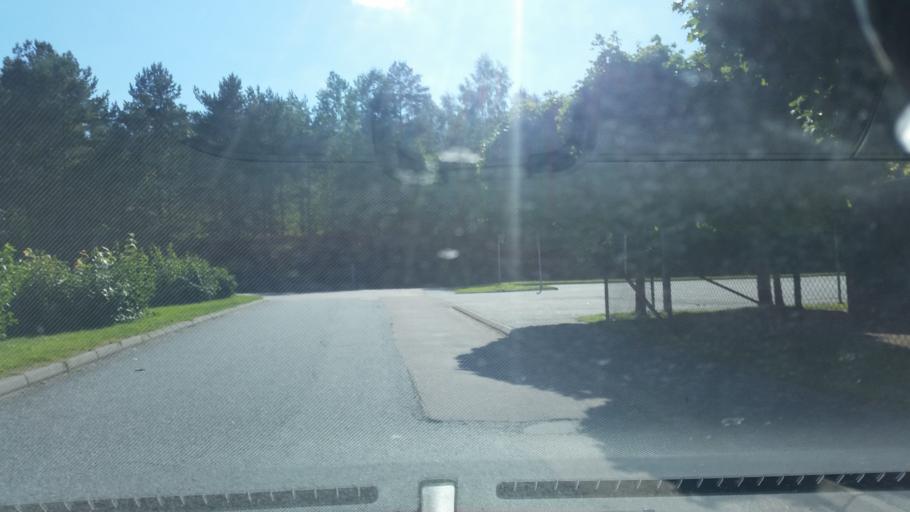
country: SE
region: Vaestra Goetaland
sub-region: Partille Kommun
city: Furulund
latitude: 57.7257
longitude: 12.1276
